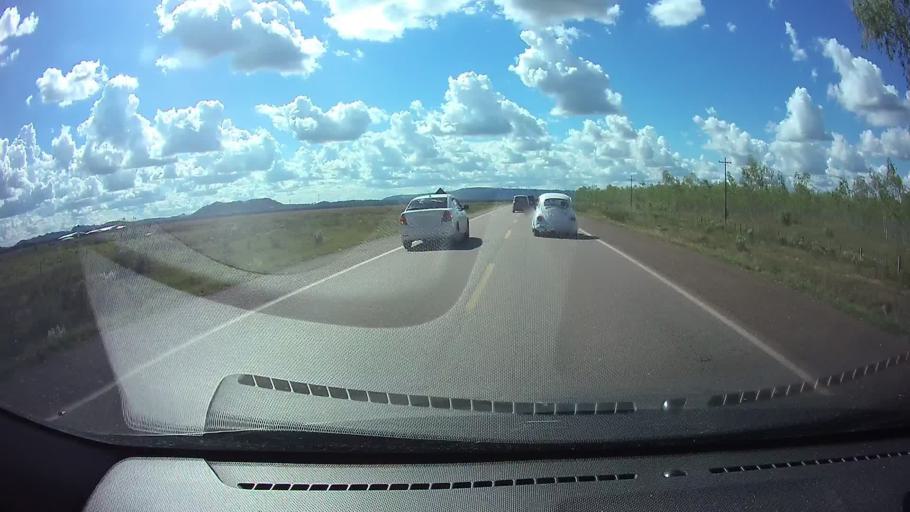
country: PY
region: Paraguari
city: Sapucai
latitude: -25.7418
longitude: -56.8094
